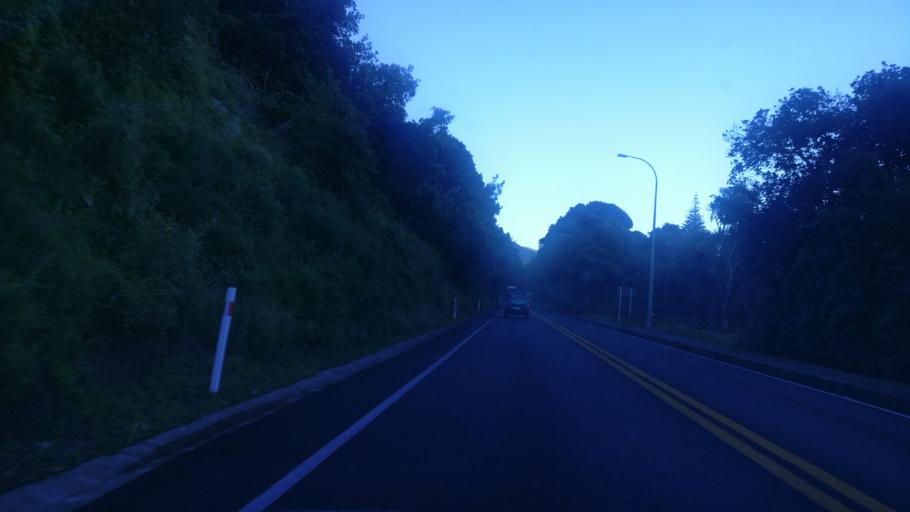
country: NZ
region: Wellington
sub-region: Kapiti Coast District
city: Paraparaumu
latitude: -40.9915
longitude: 174.9493
